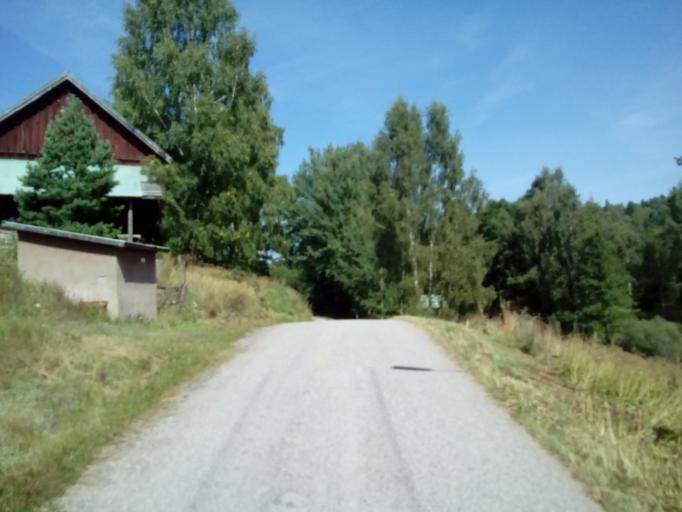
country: SE
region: Kalmar
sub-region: Vasterviks Kommun
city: Ankarsrum
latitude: 57.8281
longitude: 16.1427
